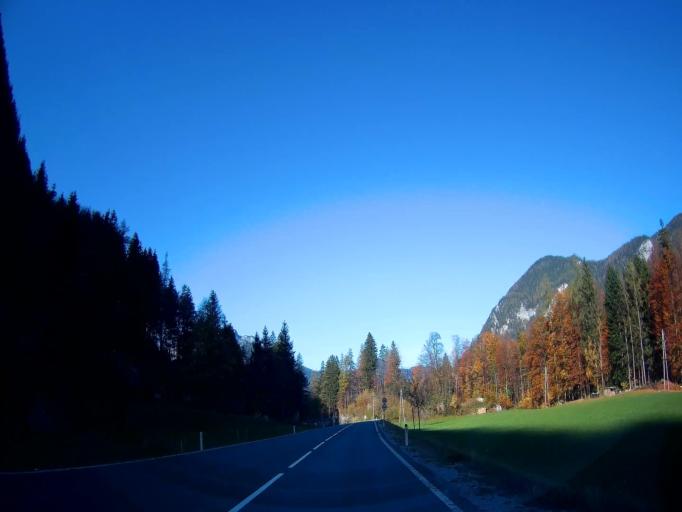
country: AT
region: Salzburg
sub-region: Politischer Bezirk Zell am See
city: Sankt Martin bei Lofer
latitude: 47.5588
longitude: 12.7183
